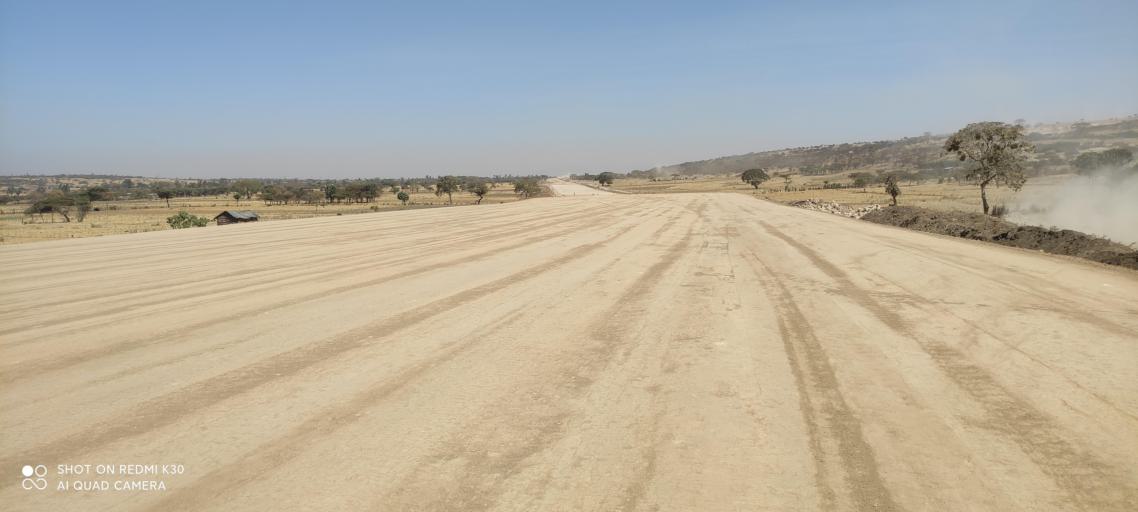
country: ET
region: Oromiya
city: Shashemene
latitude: 7.3953
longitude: 38.6583
